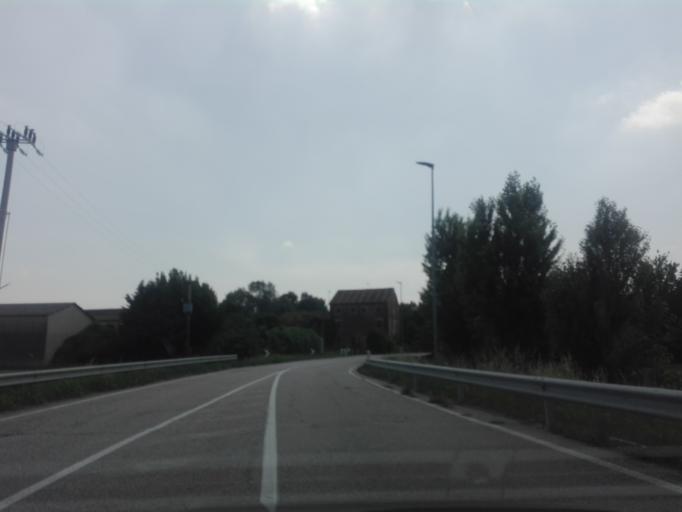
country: IT
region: Veneto
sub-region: Provincia di Rovigo
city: Villamarzana
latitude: 45.0262
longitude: 11.7096
